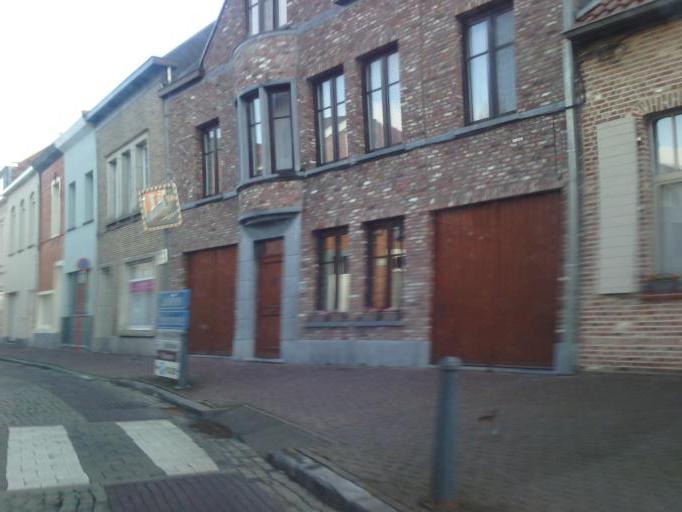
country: BE
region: Flanders
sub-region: Provincie Oost-Vlaanderen
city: Zele
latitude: 51.0706
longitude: 4.0400
